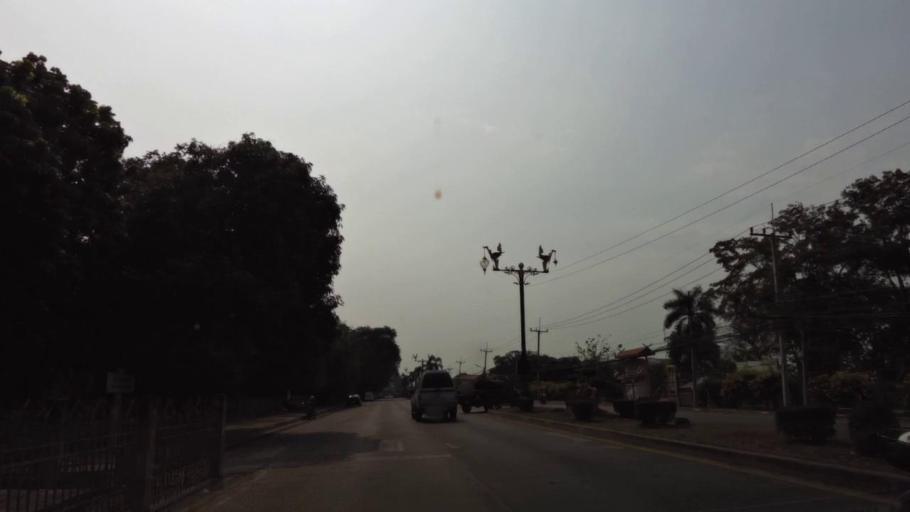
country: TH
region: Phra Nakhon Si Ayutthaya
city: Phra Nakhon Si Ayutthaya
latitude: 14.3490
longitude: 100.5618
